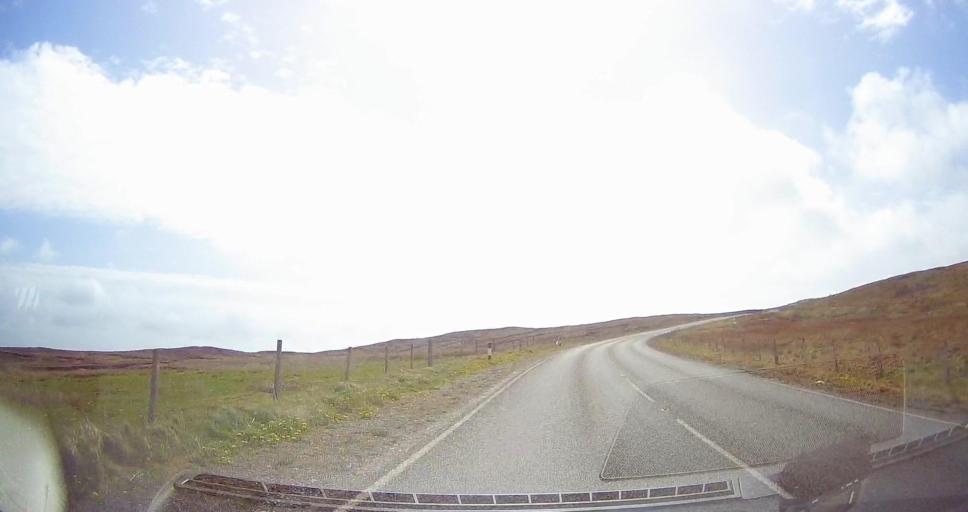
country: GB
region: Scotland
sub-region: Shetland Islands
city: Sandwick
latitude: 60.0934
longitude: -1.2295
